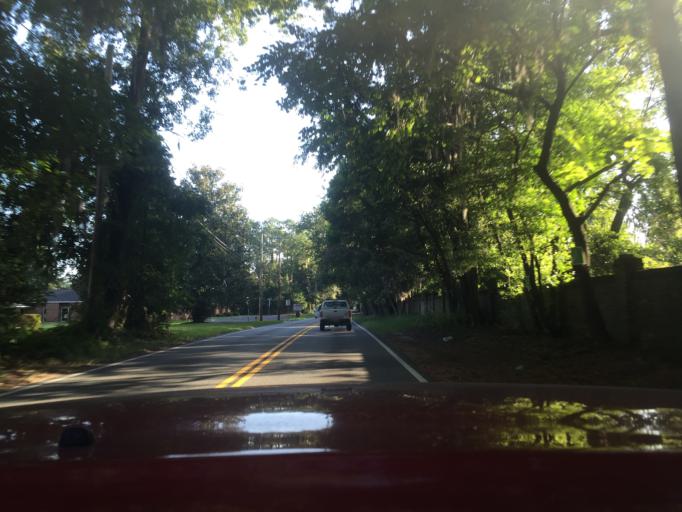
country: US
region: Georgia
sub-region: Chatham County
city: Thunderbolt
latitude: 32.0176
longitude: -81.0972
